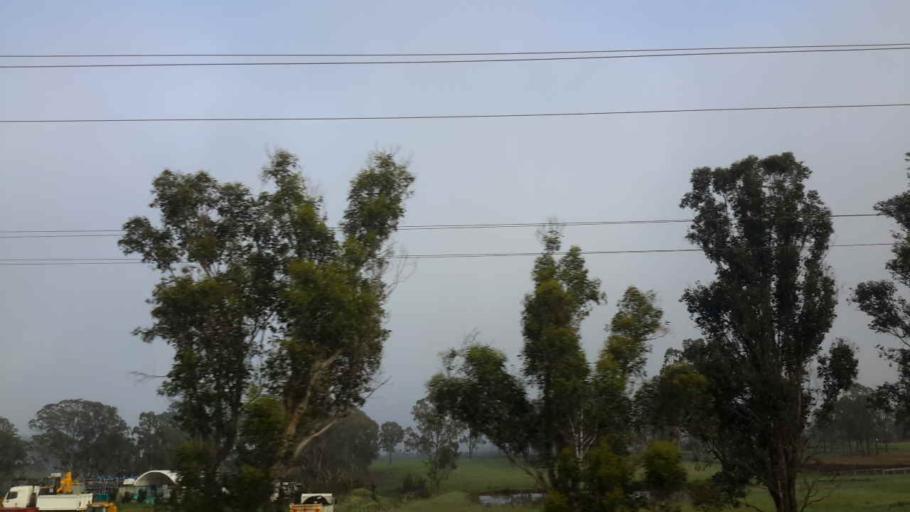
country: AU
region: New South Wales
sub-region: Penrith Municipality
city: Glenmore Park
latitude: -33.8193
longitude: 150.6867
